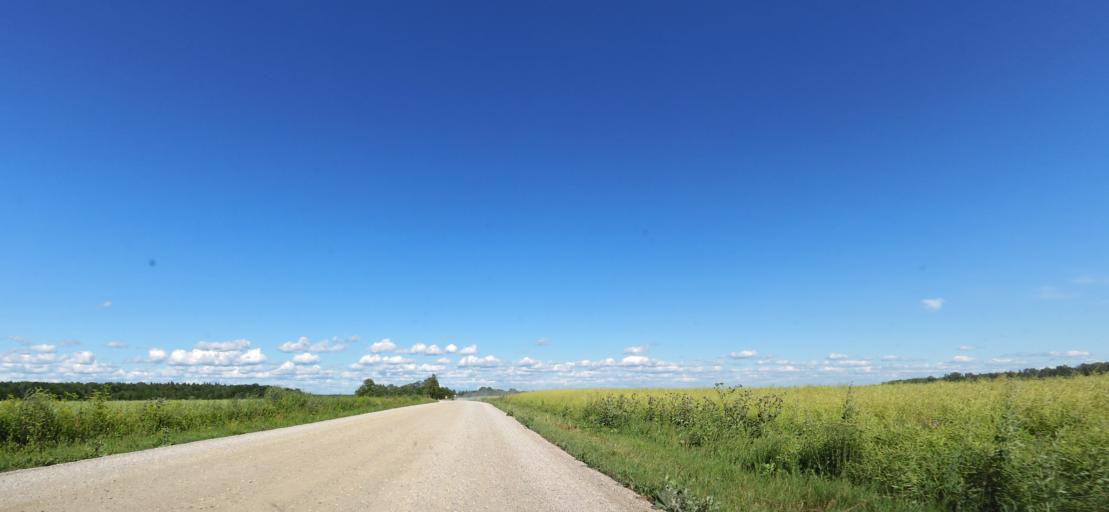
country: LT
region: Panevezys
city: Pasvalys
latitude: 56.1453
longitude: 24.4264
